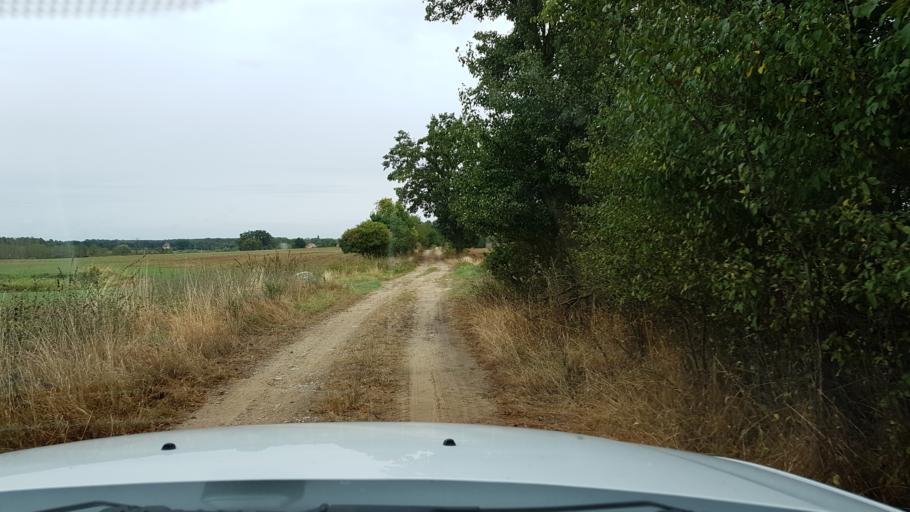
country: PL
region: West Pomeranian Voivodeship
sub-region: Powiat gryfinski
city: Chojna
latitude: 52.9017
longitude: 14.4467
